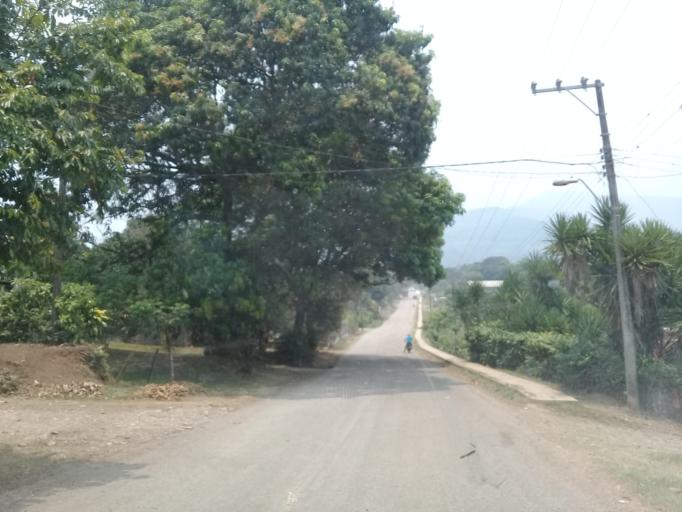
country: MX
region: Veracruz
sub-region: Tezonapa
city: Laguna Chica (Pueblo Nuevo)
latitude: 18.5392
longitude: -96.7325
